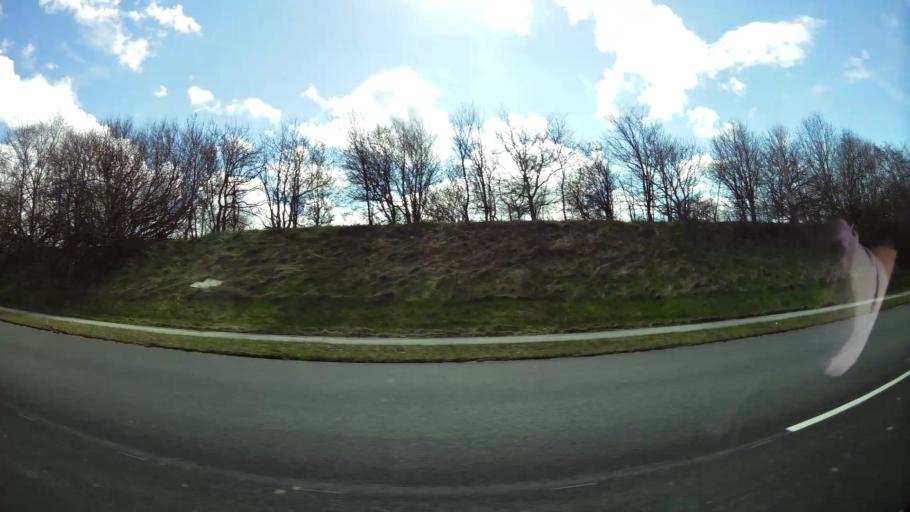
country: DK
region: North Denmark
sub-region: Hjorring Kommune
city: Hirtshals
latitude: 57.5687
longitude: 9.9772
